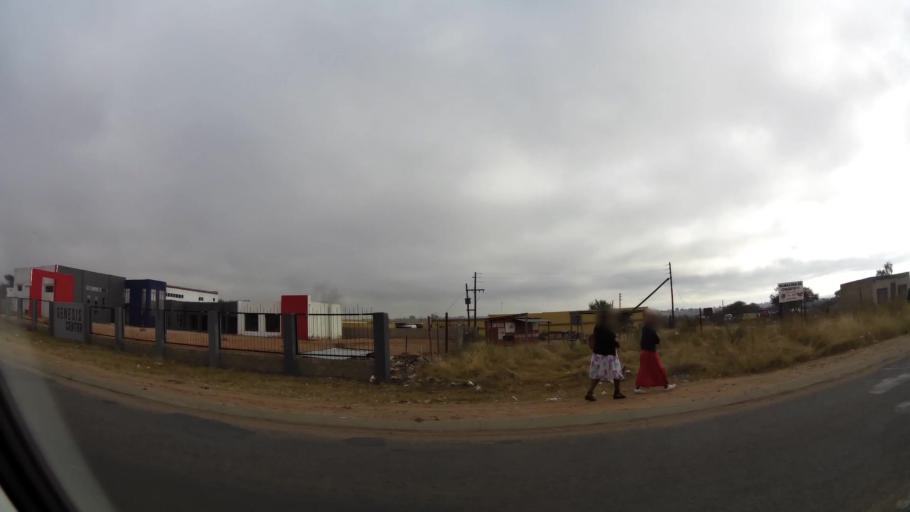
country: ZA
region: Limpopo
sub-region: Capricorn District Municipality
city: Polokwane
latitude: -23.8337
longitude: 29.3810
